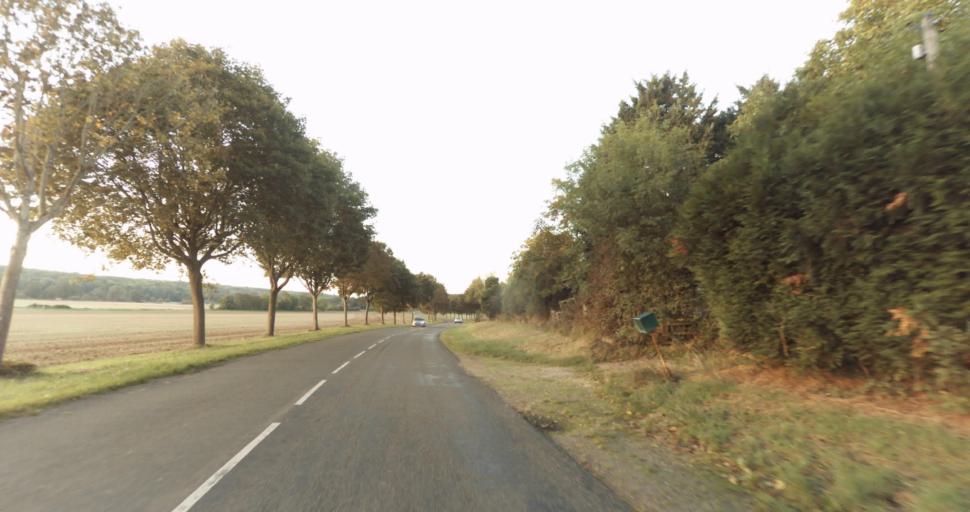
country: FR
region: Centre
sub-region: Departement d'Eure-et-Loir
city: Garnay
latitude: 48.7151
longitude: 1.3449
